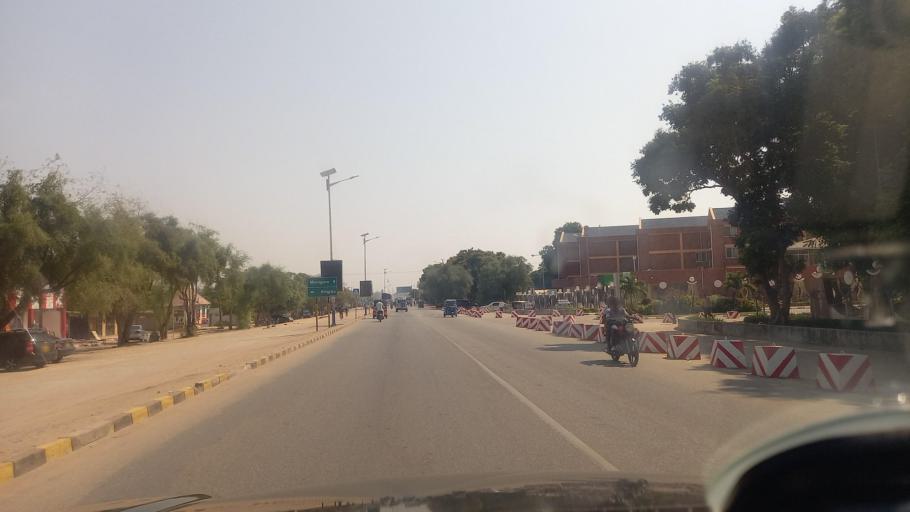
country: TZ
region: Dodoma
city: Dodoma
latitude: -6.1791
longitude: 35.7562
